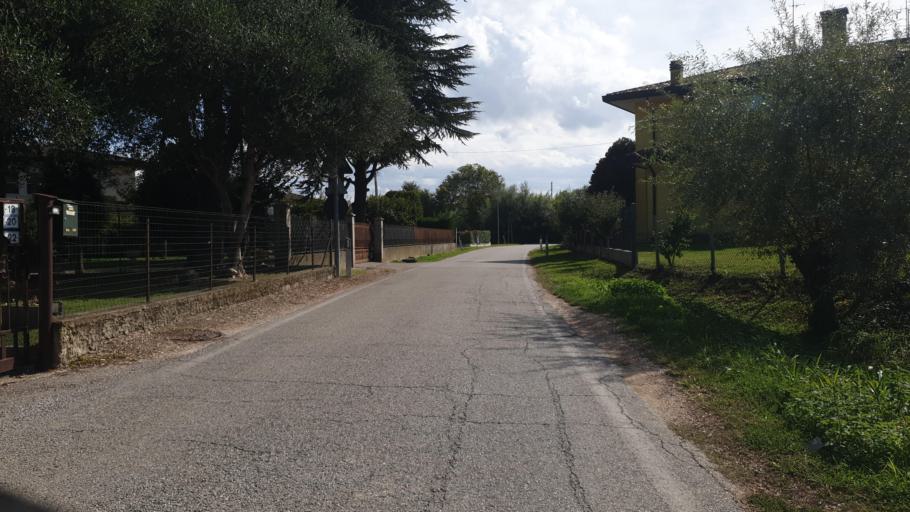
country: IT
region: Veneto
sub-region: Provincia di Padova
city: Arzergrande
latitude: 45.2765
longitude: 12.0552
